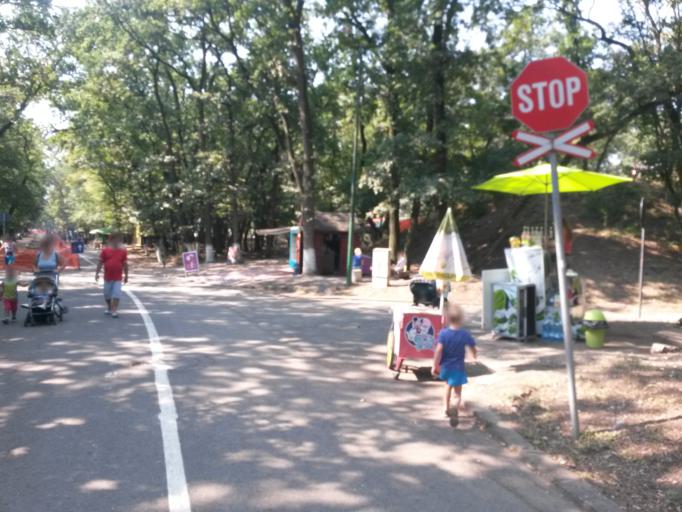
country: RO
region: Mures
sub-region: Comuna Sangeorgiu de Mures
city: Sangeorgiu de Mures
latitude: 46.5508
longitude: 24.5888
